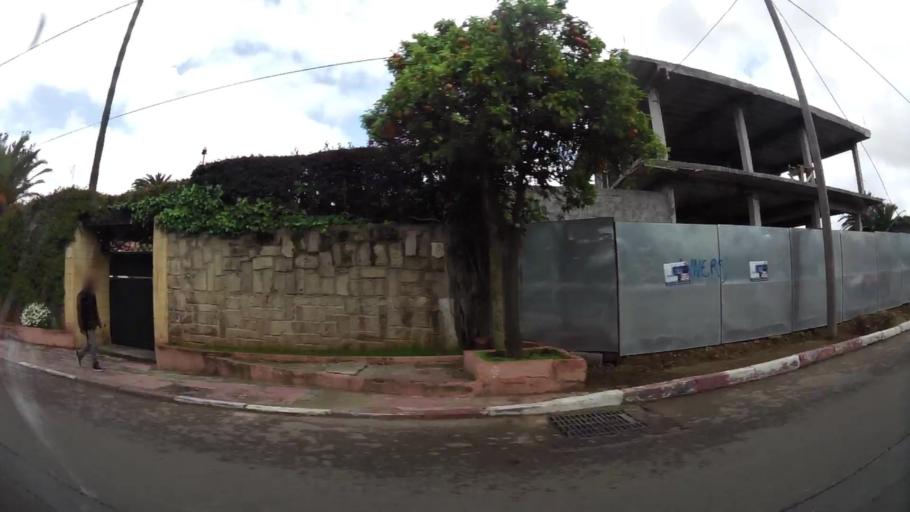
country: MA
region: Grand Casablanca
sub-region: Casablanca
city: Casablanca
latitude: 33.5506
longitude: -7.6152
